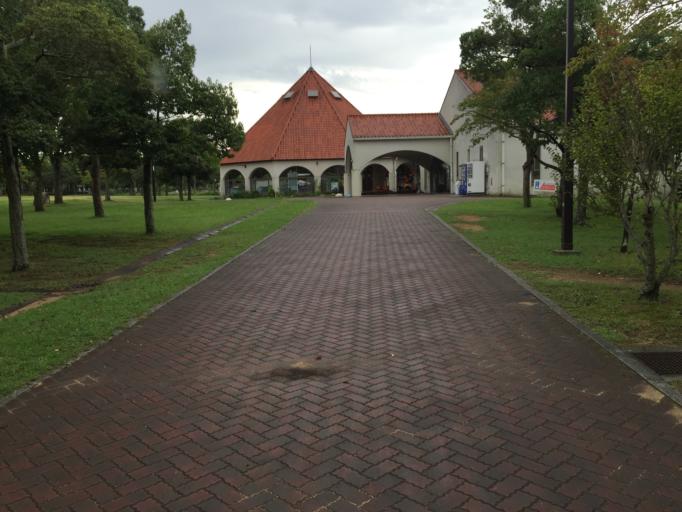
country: JP
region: Hyogo
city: Kobe
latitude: 34.7096
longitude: 135.1125
